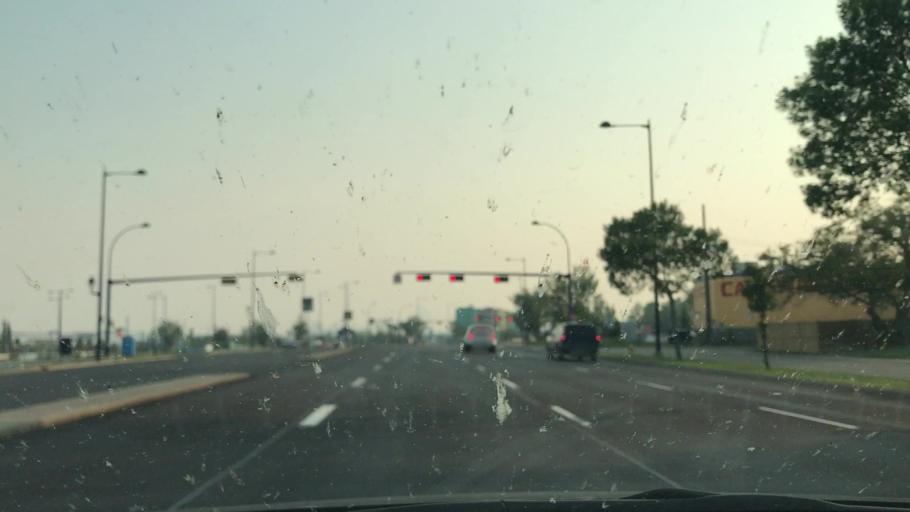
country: CA
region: Alberta
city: Edmonton
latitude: 53.5890
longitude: -113.4352
